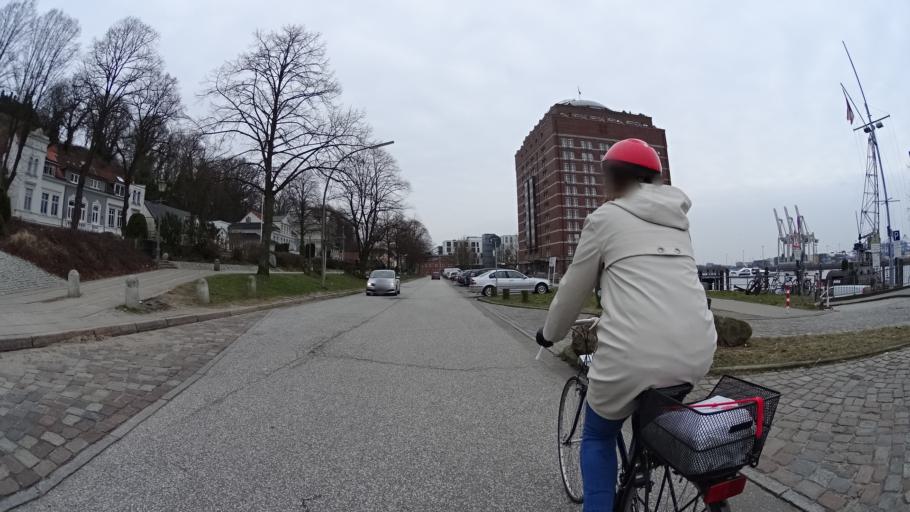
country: DE
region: Hamburg
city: Altona
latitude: 53.5447
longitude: 9.9152
